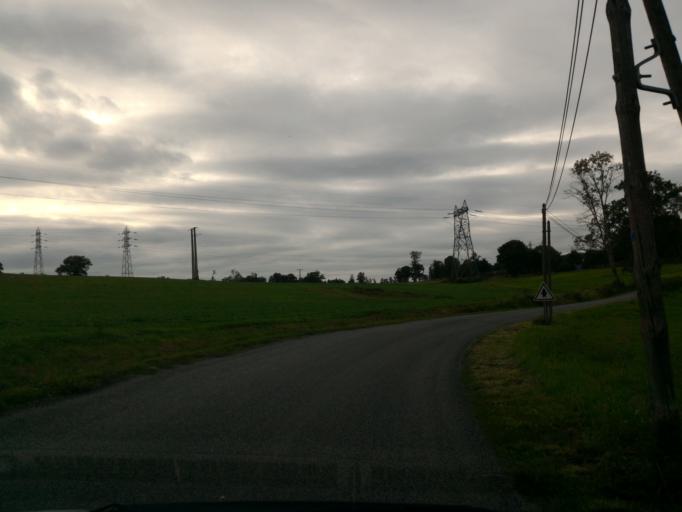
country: FR
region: Poitou-Charentes
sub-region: Departement de la Charente
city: Brigueuil
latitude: 45.9089
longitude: 0.8588
